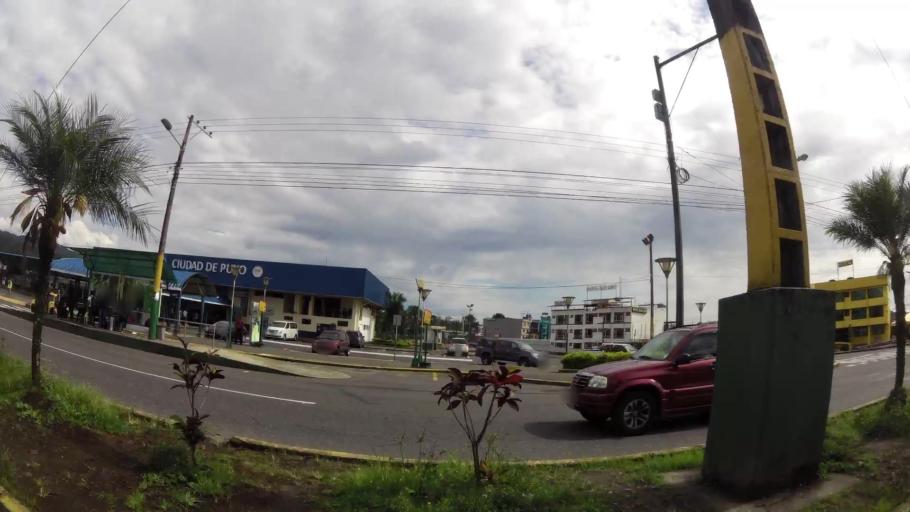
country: EC
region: Pastaza
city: Puyo
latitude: -1.4906
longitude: -78.0059
